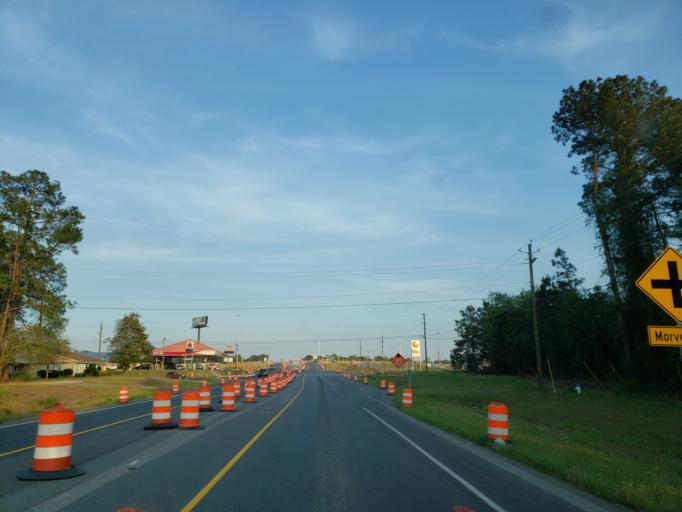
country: US
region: Georgia
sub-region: Lowndes County
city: Hahira
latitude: 30.9934
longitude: -83.3923
